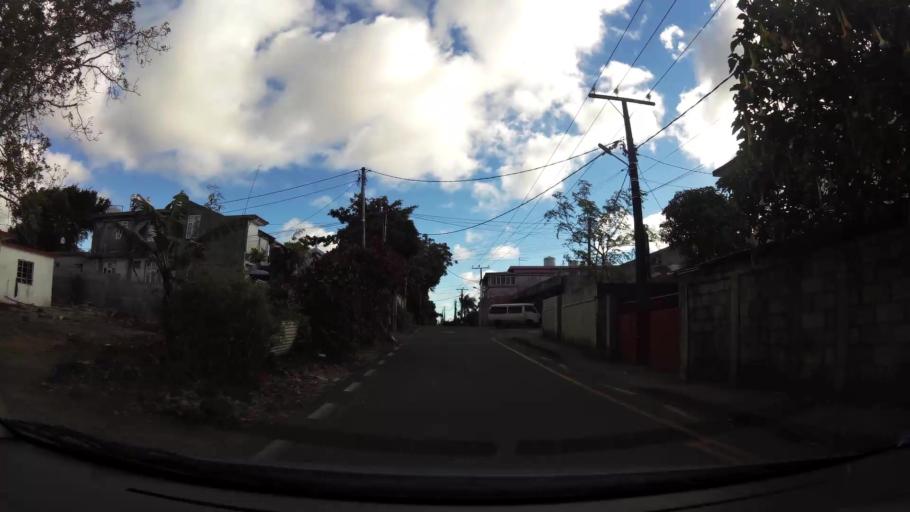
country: MU
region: Plaines Wilhems
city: Curepipe
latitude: -20.2979
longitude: 57.5101
